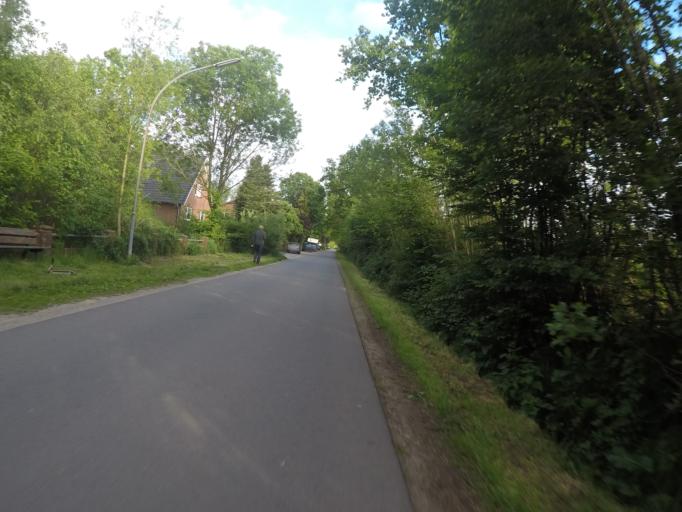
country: DE
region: Schleswig-Holstein
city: Bonningstedt
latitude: 53.6891
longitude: 9.9234
